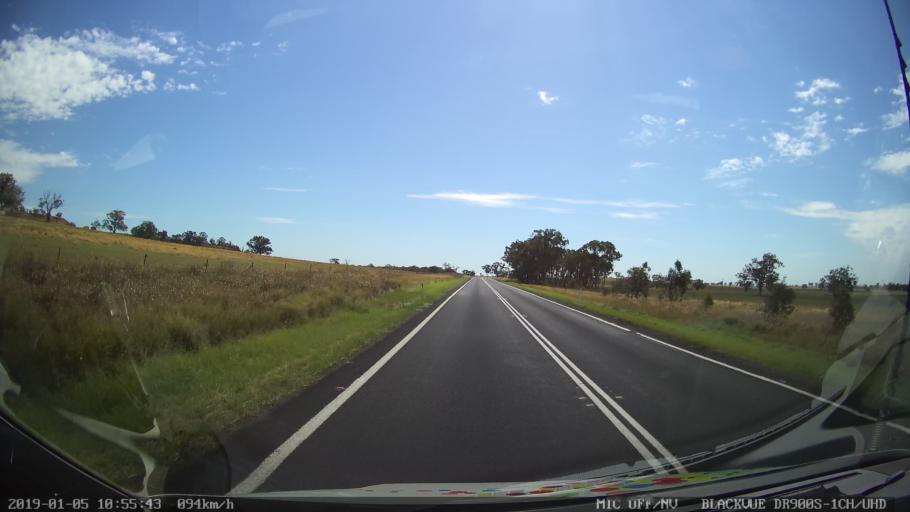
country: AU
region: New South Wales
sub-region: Warrumbungle Shire
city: Coonabarabran
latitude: -31.4465
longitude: 149.1480
